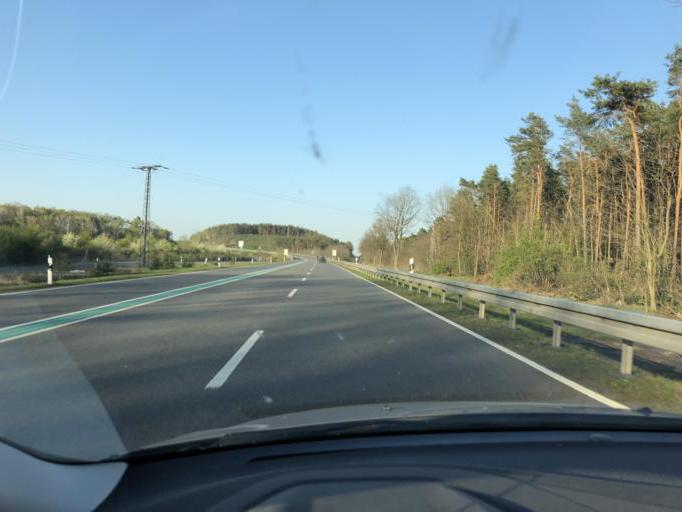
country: DE
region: Brandenburg
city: Schwarzbach
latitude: 51.4876
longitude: 13.9351
